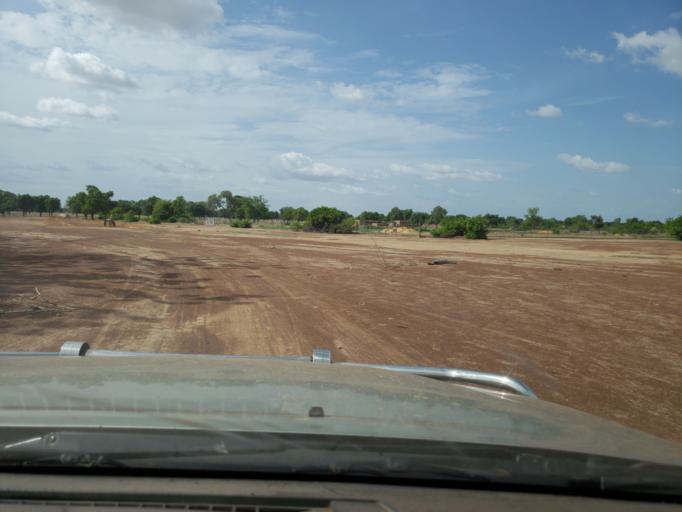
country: ML
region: Segou
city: Bla
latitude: 12.7880
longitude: -5.6047
